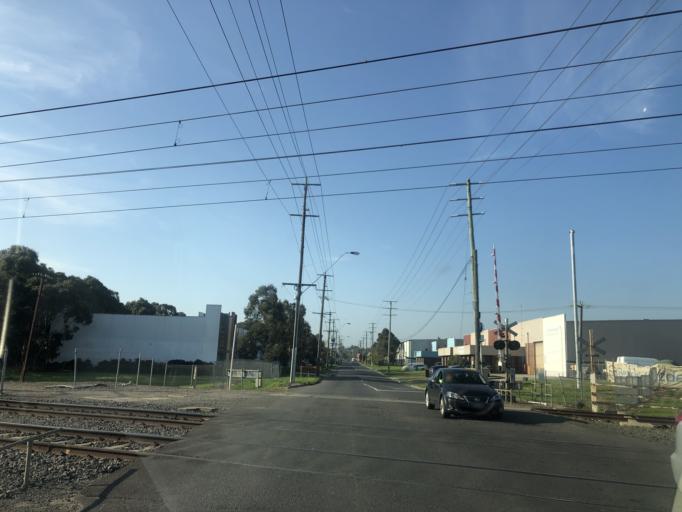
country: AU
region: Victoria
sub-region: Casey
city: Doveton
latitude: -38.0063
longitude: 145.2357
